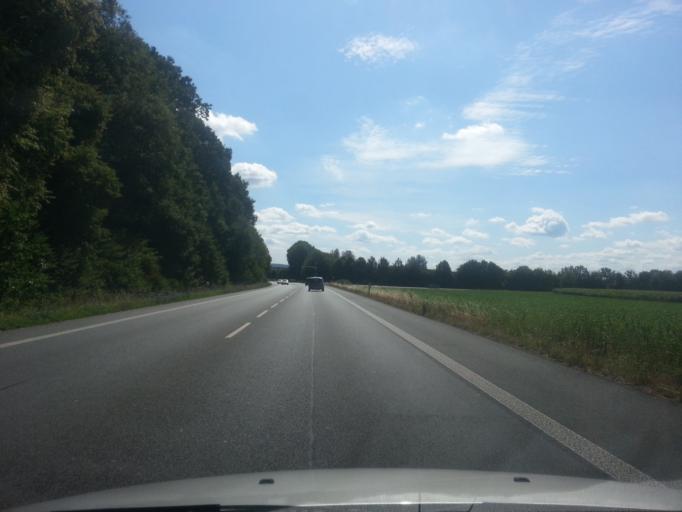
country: DE
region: Hesse
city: Dieburg
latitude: 49.8885
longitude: 8.8708
